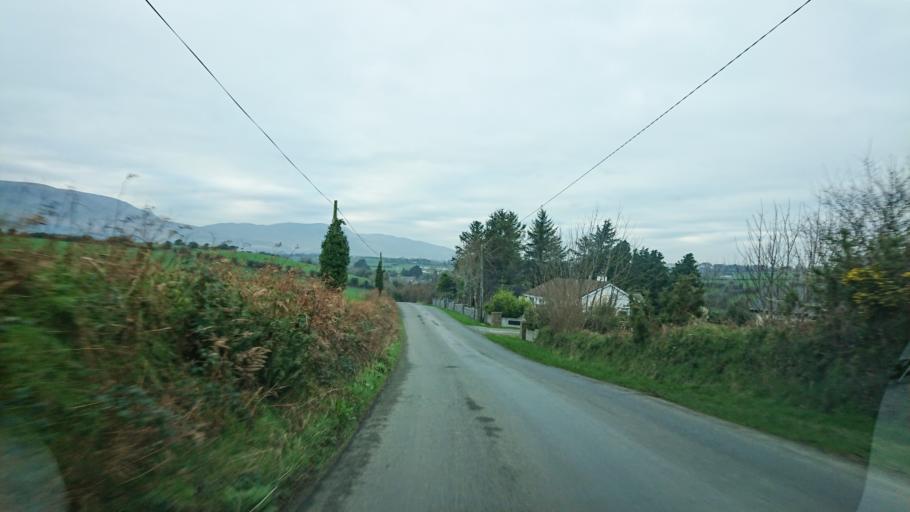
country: IE
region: Munster
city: Carrick-on-Suir
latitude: 52.2775
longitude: -7.4269
